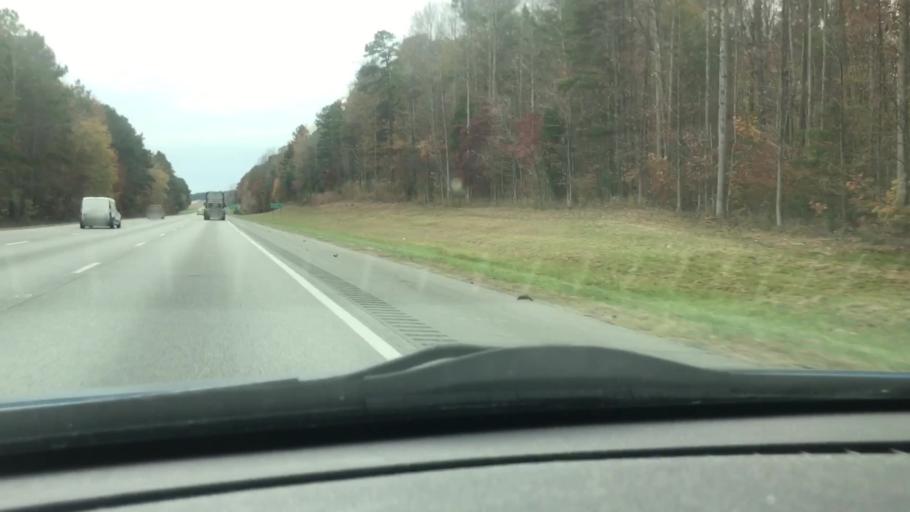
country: US
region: North Carolina
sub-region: Davidson County
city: Lexington
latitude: 35.8039
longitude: -80.1930
